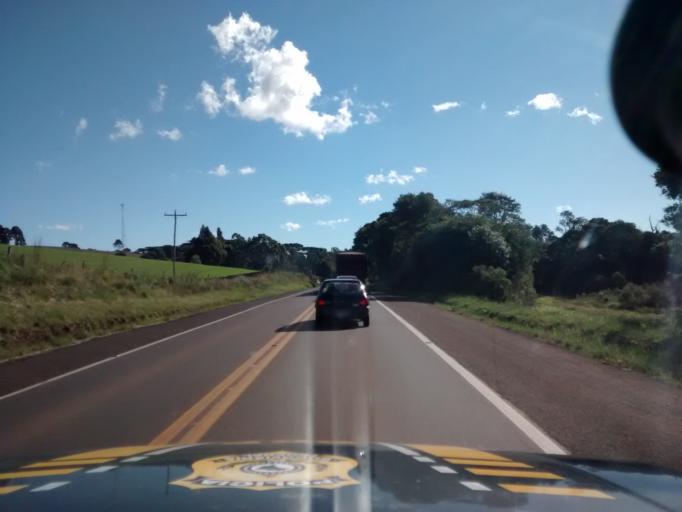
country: BR
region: Rio Grande do Sul
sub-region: Lagoa Vermelha
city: Lagoa Vermelha
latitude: -28.2984
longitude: -51.4539
